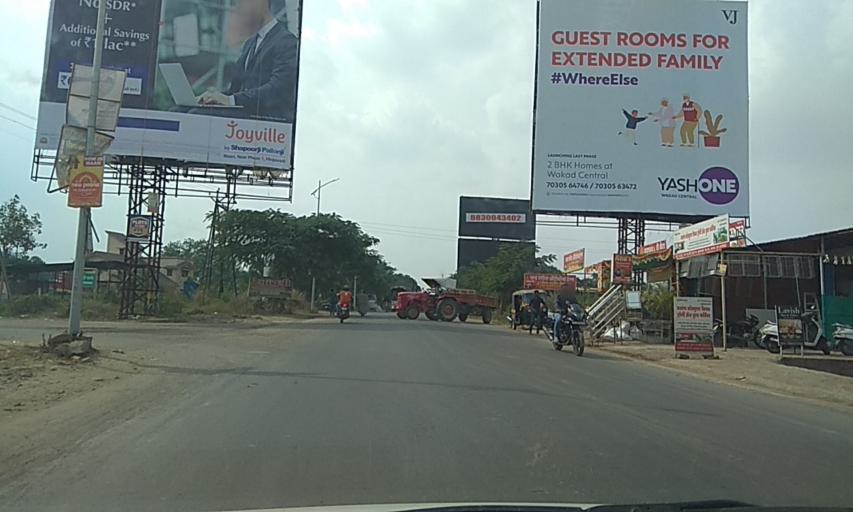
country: IN
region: Maharashtra
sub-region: Pune Division
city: Pimpri
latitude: 18.5807
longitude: 73.7214
